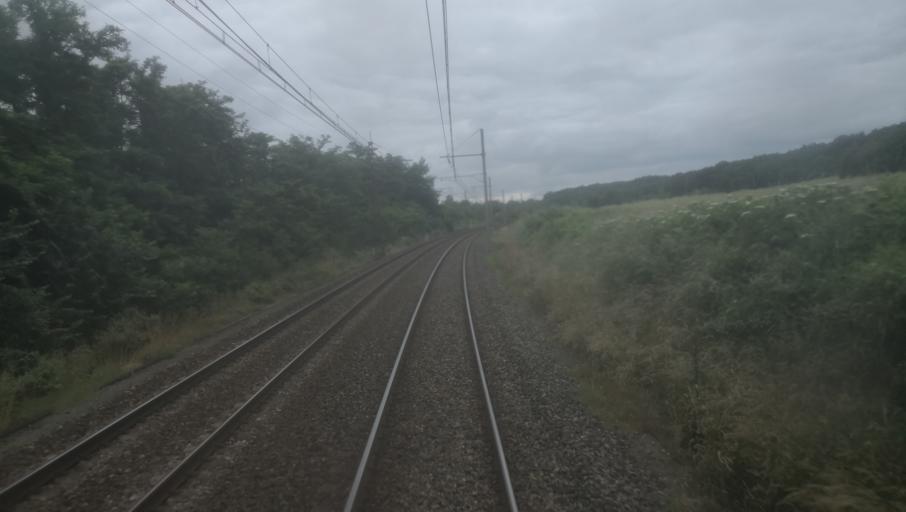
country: FR
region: Midi-Pyrenees
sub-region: Departement du Tarn-et-Garonne
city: Verdun-sur-Garonne
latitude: 43.8747
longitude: 1.2703
